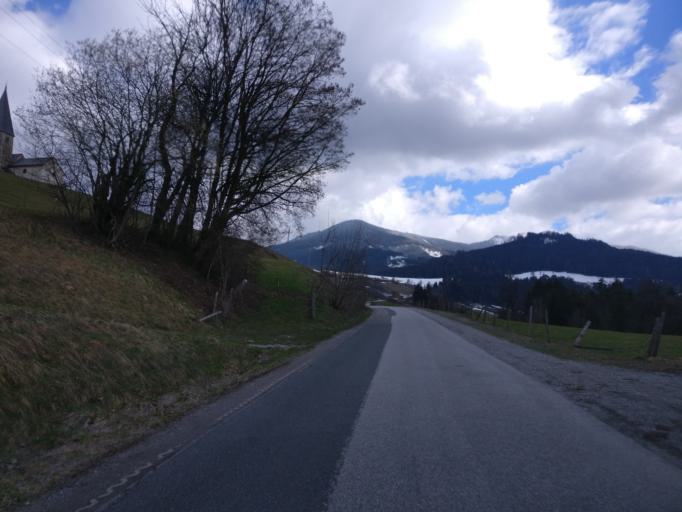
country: AT
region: Salzburg
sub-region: Politischer Bezirk Sankt Johann im Pongau
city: Bischofshofen
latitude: 47.4272
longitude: 13.2296
